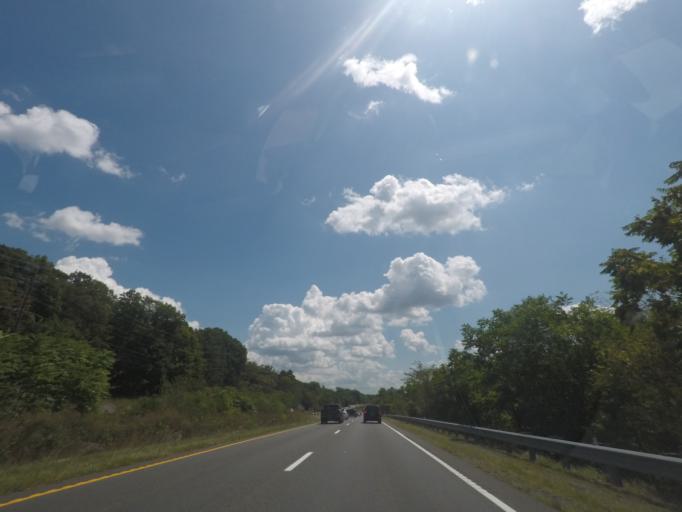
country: US
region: Virginia
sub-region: City of Winchester
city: Winchester
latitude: 39.1554
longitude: -78.1419
